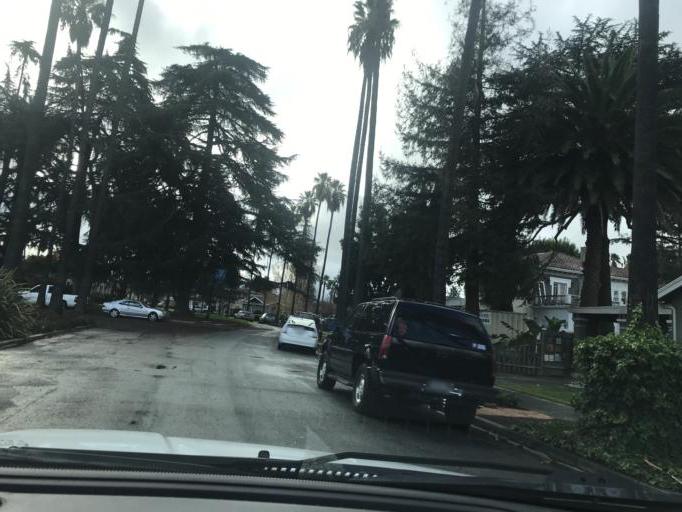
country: US
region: California
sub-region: Santa Clara County
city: Buena Vista
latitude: 37.3164
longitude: -121.9011
